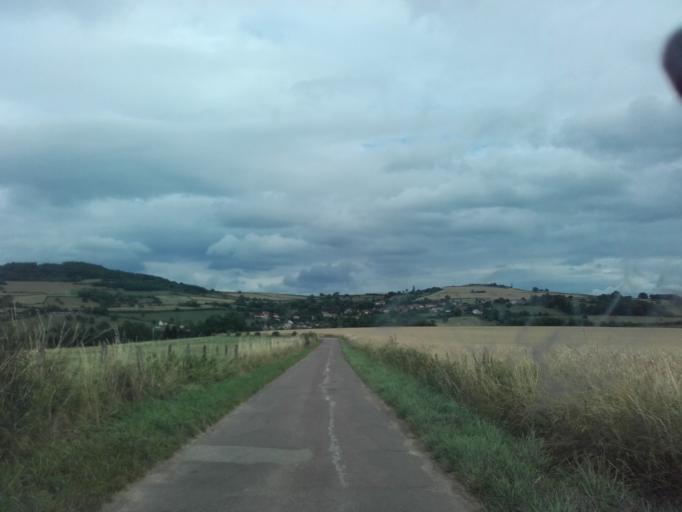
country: FR
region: Bourgogne
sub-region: Departement de Saone-et-Loire
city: Saint-Leger-sur-Dheune
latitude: 46.8828
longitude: 4.6540
